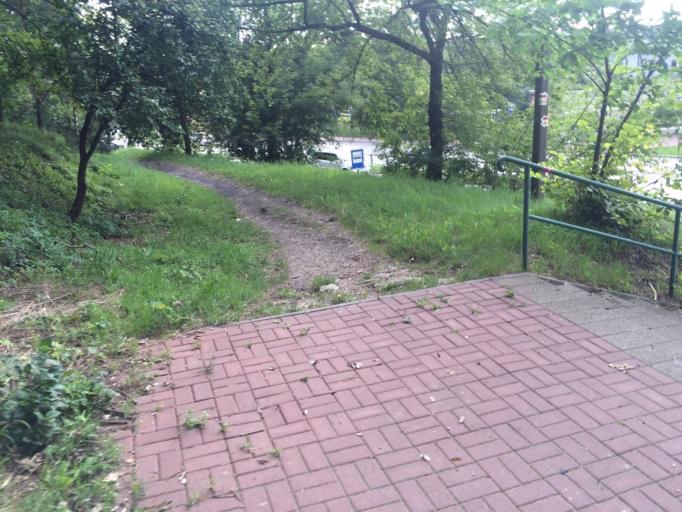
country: PL
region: Swietokrzyskie
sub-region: Powiat starachowicki
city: Starachowice
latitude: 51.0516
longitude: 21.0642
